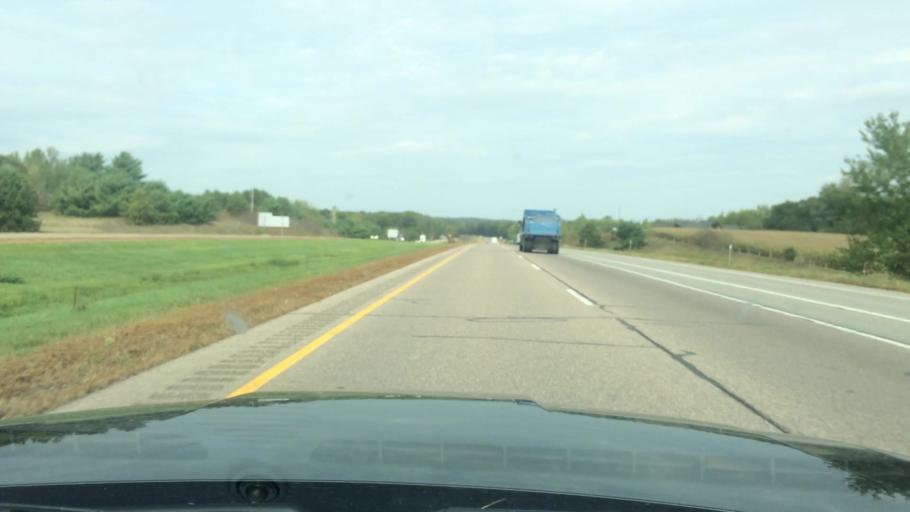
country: US
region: Wisconsin
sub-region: Marathon County
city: Mosinee
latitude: 44.6794
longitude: -89.6414
